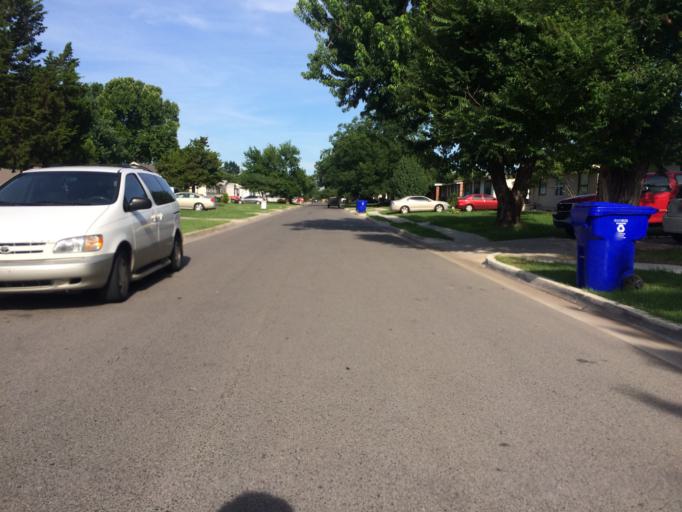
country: US
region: Oklahoma
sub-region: Cleveland County
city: Norman
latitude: 35.2244
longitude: -97.4617
